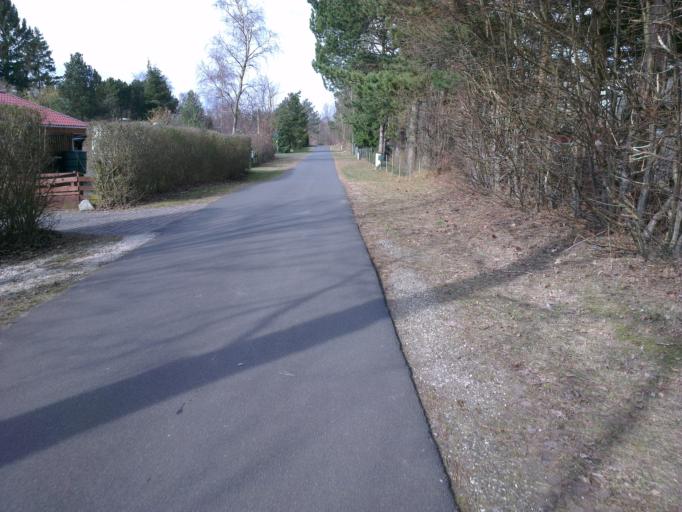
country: DK
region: Capital Region
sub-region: Halsnaes Kommune
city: Hundested
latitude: 55.9206
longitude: 11.9081
